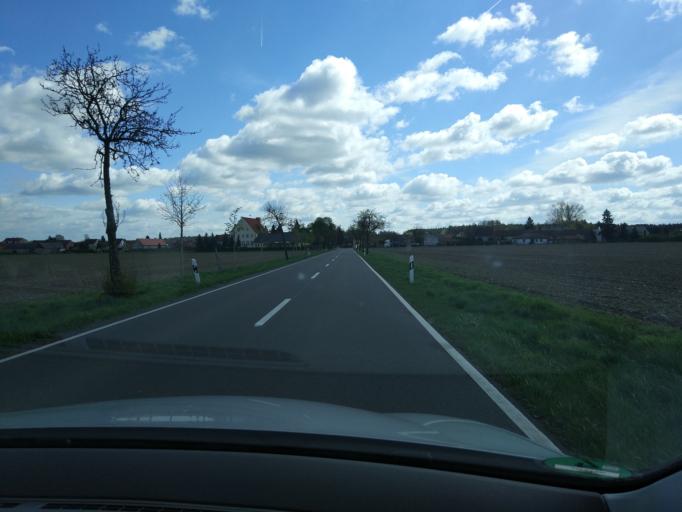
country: DE
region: Saxony-Anhalt
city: Radis
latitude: 51.7852
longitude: 12.4824
